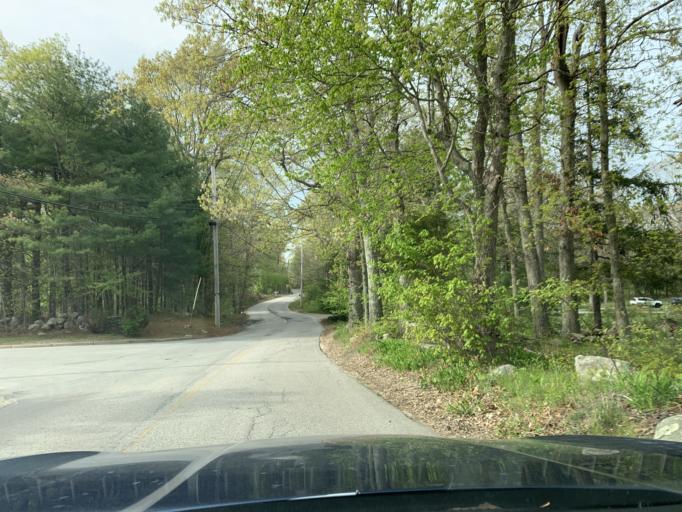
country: US
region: Rhode Island
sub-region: Kent County
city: West Warwick
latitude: 41.6466
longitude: -71.5505
